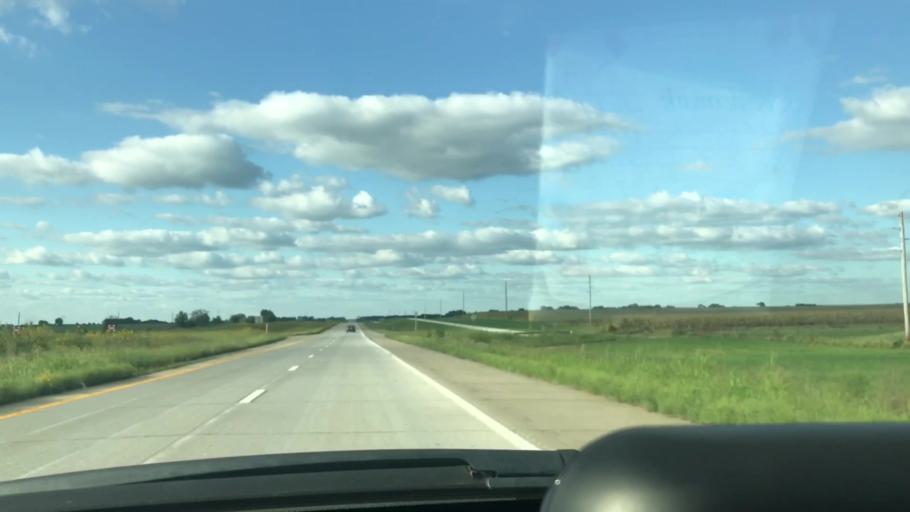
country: US
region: Missouri
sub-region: Benton County
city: Cole Camp
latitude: 38.5042
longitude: -93.2728
